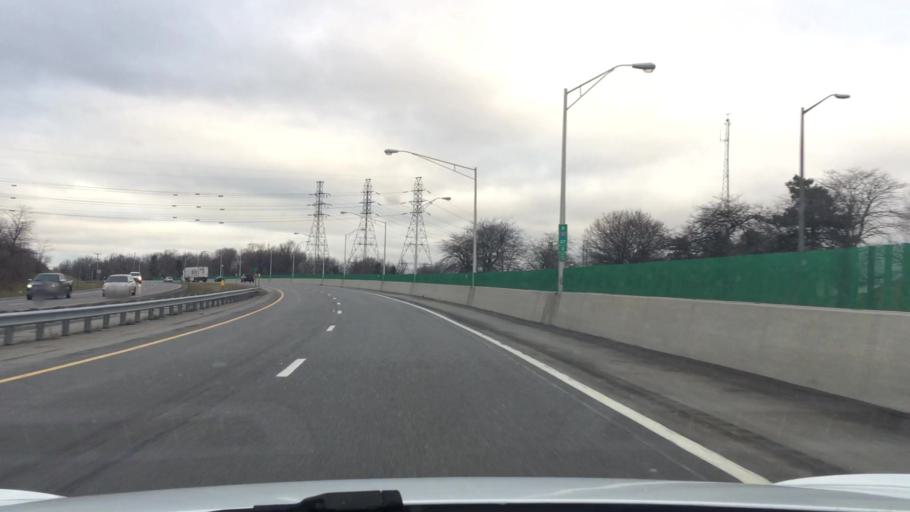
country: US
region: New York
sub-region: Niagara County
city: Lewiston
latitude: 43.1447
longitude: -79.0222
